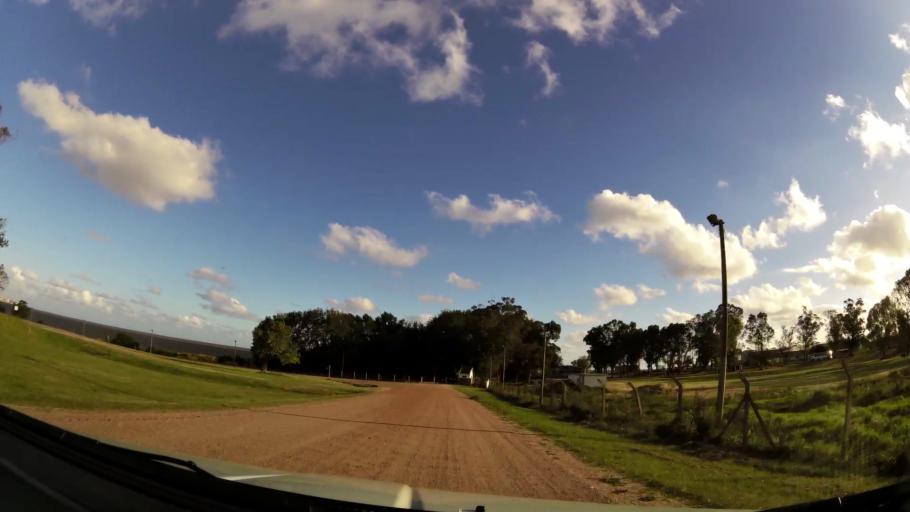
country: UY
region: Montevideo
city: Montevideo
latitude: -34.8978
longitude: -56.2610
